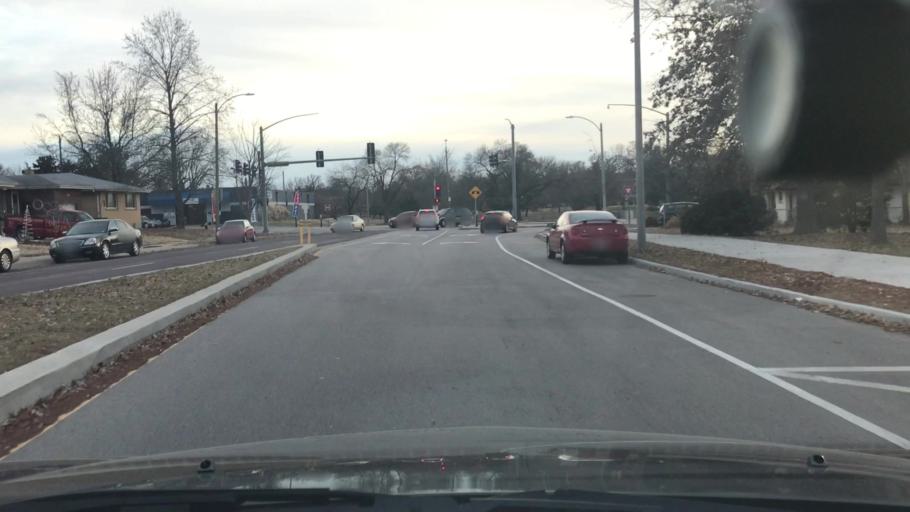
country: US
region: Missouri
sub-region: Saint Louis County
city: Shrewsbury
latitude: 38.5928
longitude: -90.3164
